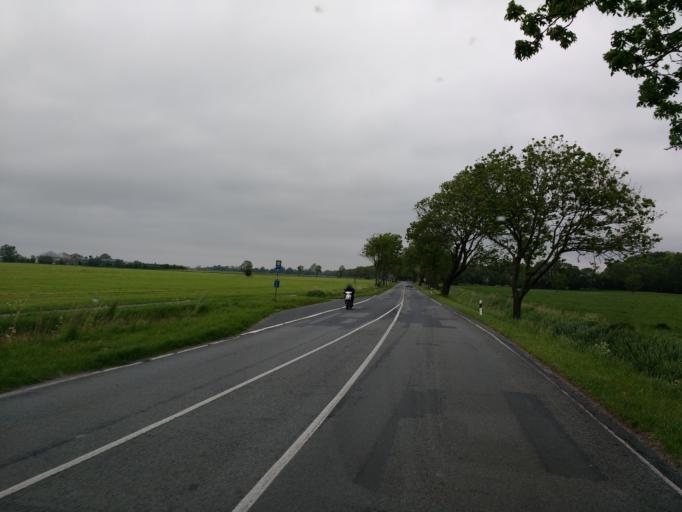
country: DE
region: Lower Saxony
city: Jever
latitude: 53.6122
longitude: 7.9328
